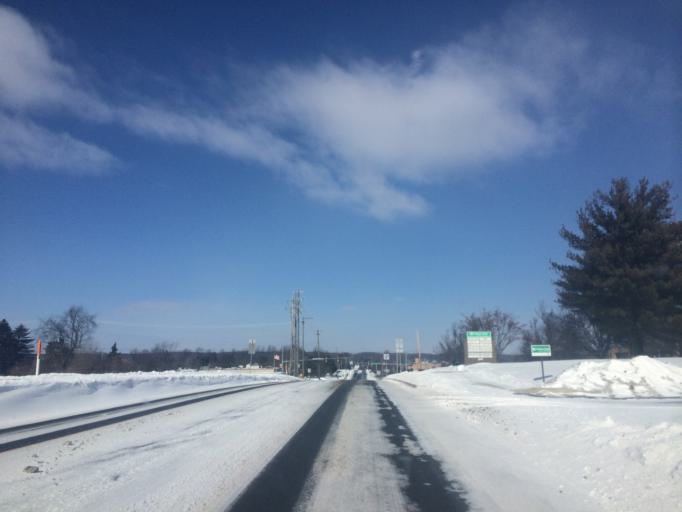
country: US
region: Pennsylvania
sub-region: Centre County
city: Park Forest Village
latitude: 40.7774
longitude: -77.8952
